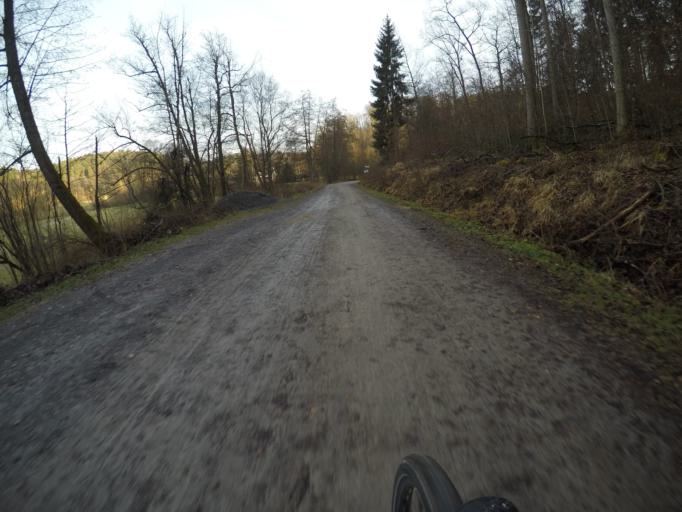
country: DE
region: Baden-Wuerttemberg
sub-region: Regierungsbezirk Stuttgart
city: Waldenbuch
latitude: 48.6429
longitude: 9.1102
